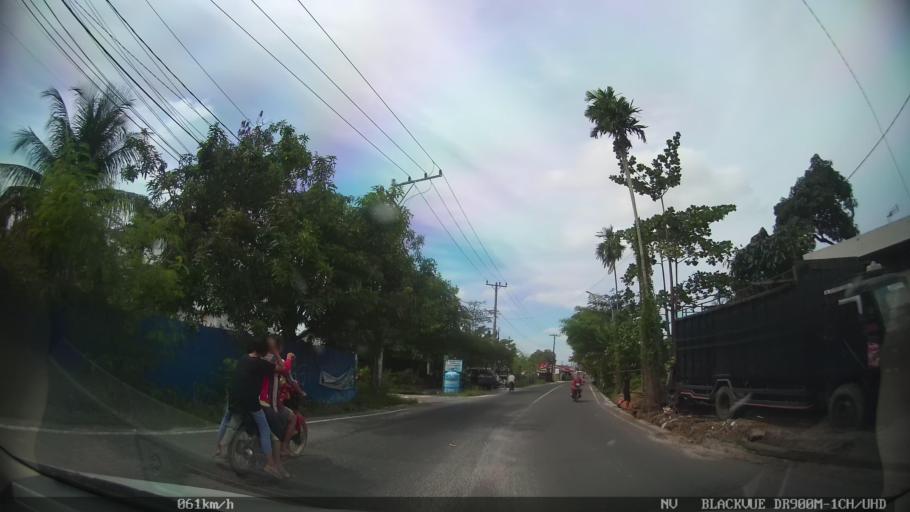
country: ID
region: North Sumatra
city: Percut
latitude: 3.5920
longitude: 98.8583
